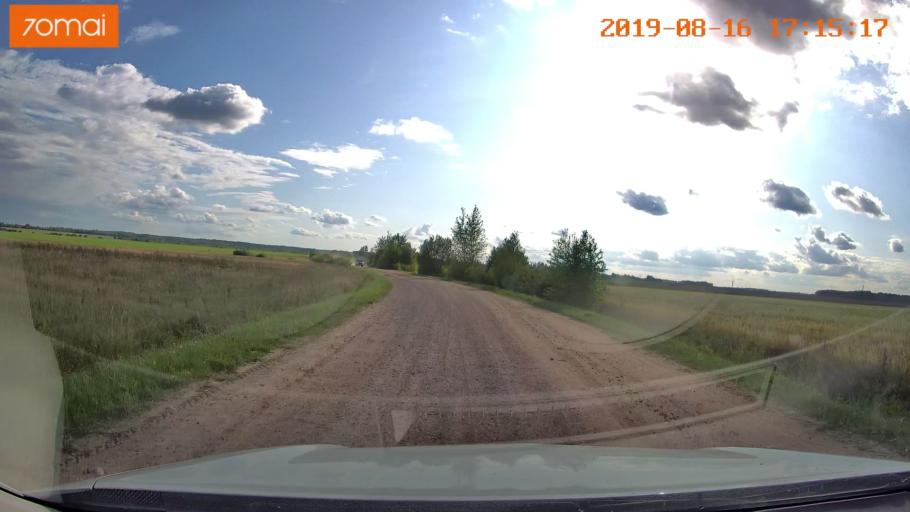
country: BY
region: Mogilev
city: Hlusha
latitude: 53.1799
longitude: 28.8453
